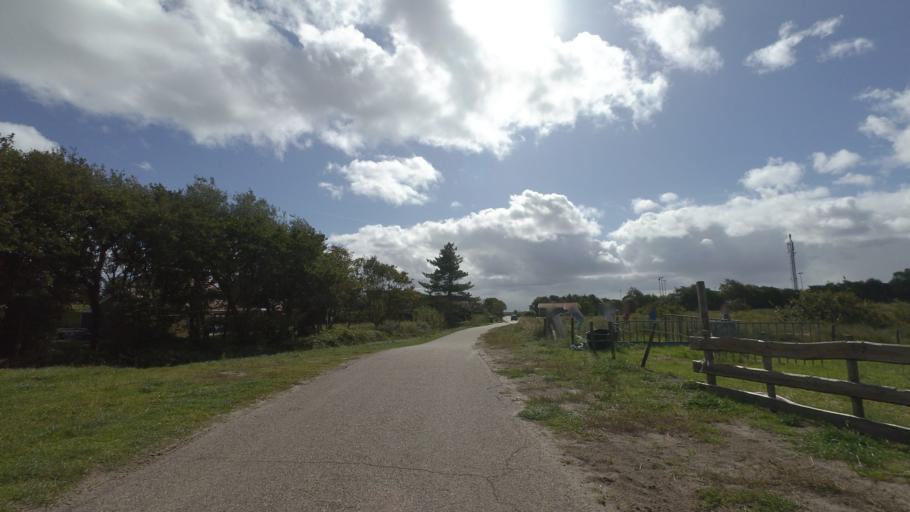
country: NL
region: Friesland
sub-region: Gemeente Ameland
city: Nes
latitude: 53.4495
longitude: 5.7936
